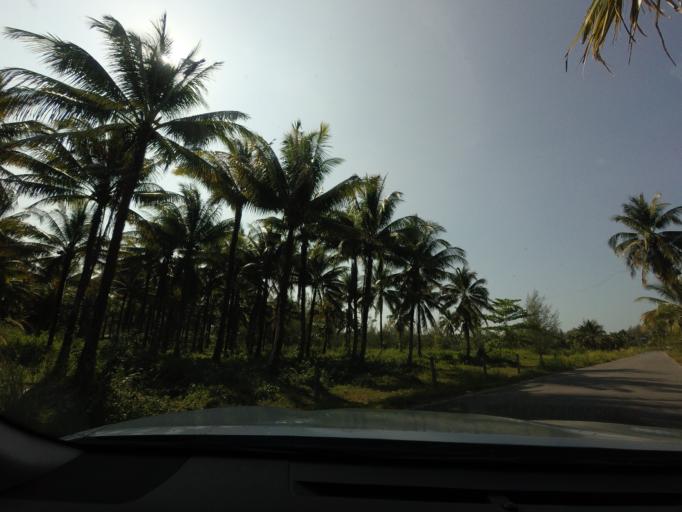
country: TH
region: Phangnga
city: Ban Khao Lak
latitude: 8.7282
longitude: 98.2411
